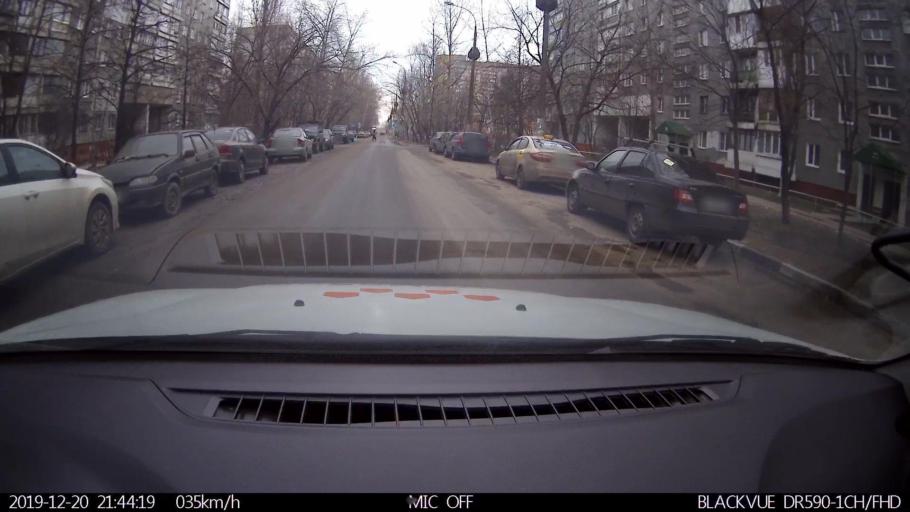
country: RU
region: Nizjnij Novgorod
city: Nizhniy Novgorod
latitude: 56.3334
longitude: 43.9367
